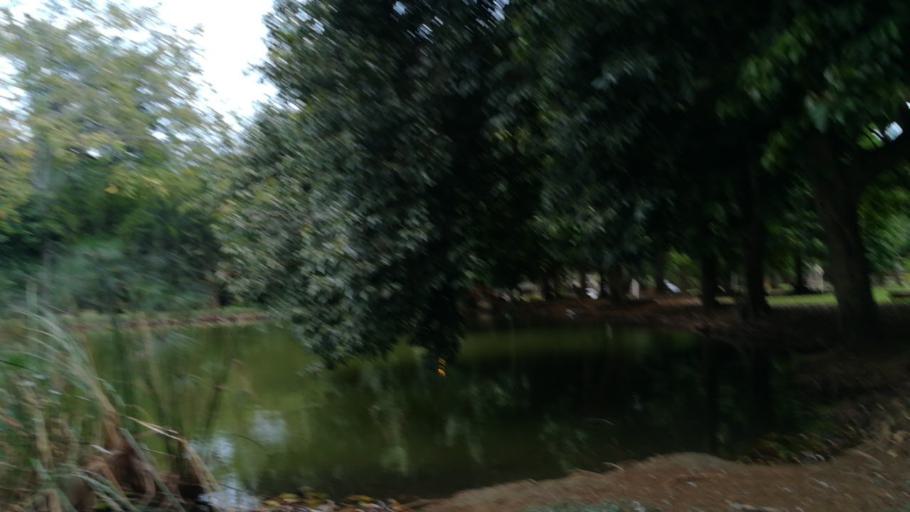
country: CO
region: Valle del Cauca
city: Cali
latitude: 3.3732
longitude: -76.5340
